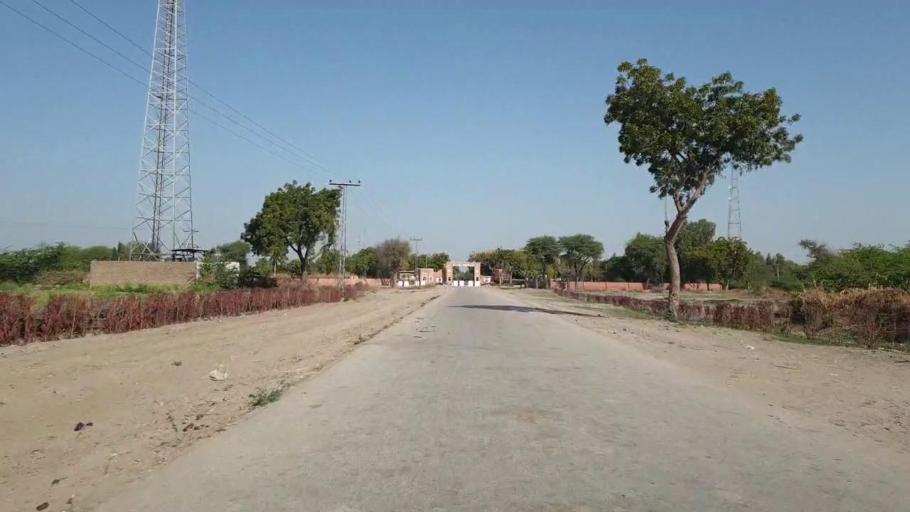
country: PK
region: Sindh
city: Chor
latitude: 25.5012
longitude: 69.7794
